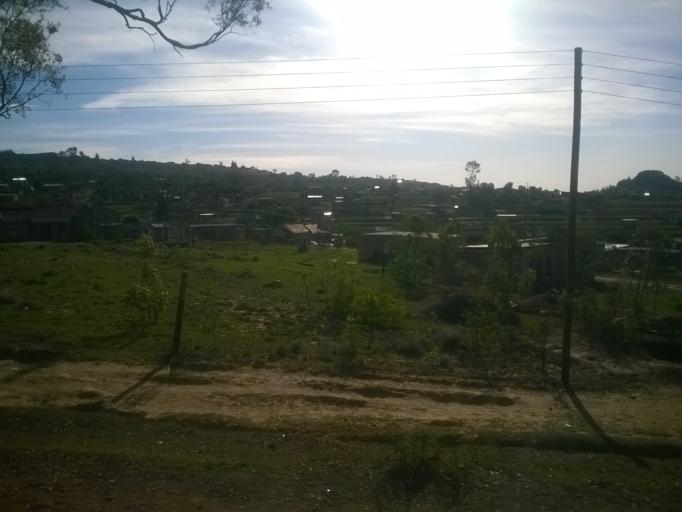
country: LS
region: Berea
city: Teyateyaneng
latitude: -29.1305
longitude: 27.7576
